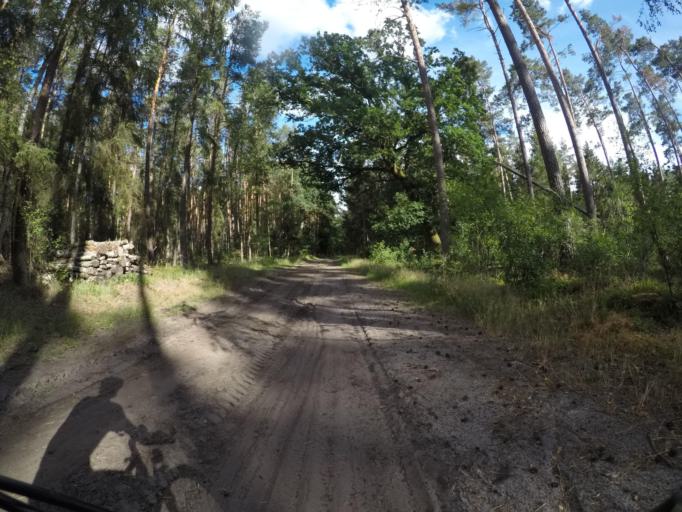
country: DE
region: Lower Saxony
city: Neu Darchau
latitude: 53.2691
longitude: 10.9824
